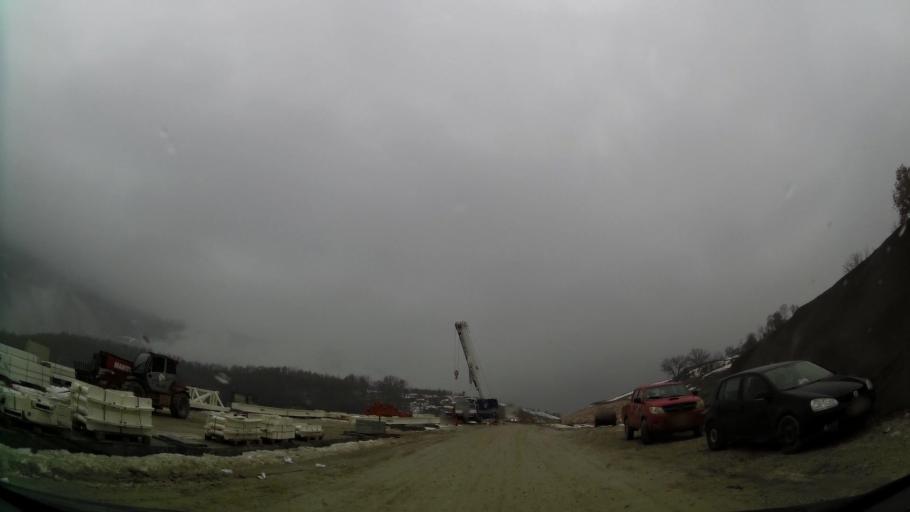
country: XK
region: Ferizaj
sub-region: Hani i Elezit
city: Hani i Elezit
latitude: 42.1662
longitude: 21.2824
